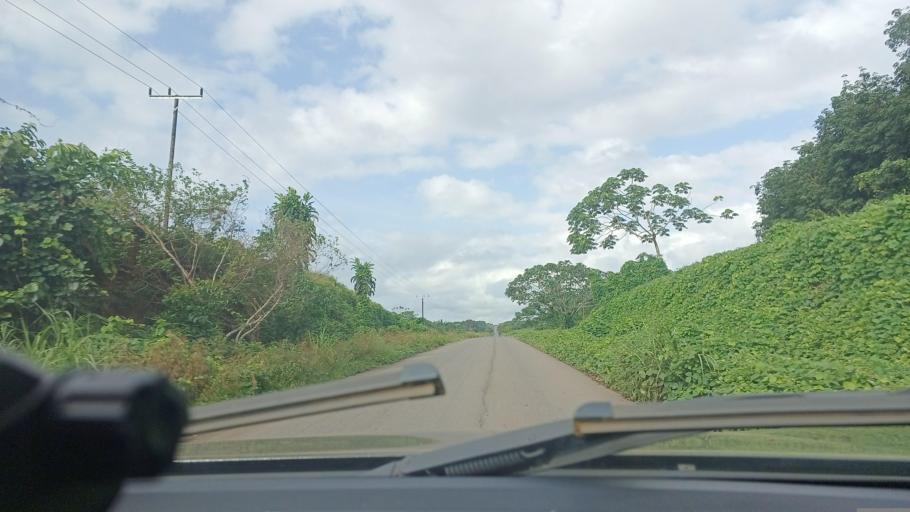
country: LR
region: Bomi
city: Tubmanburg
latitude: 6.7298
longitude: -11.0159
